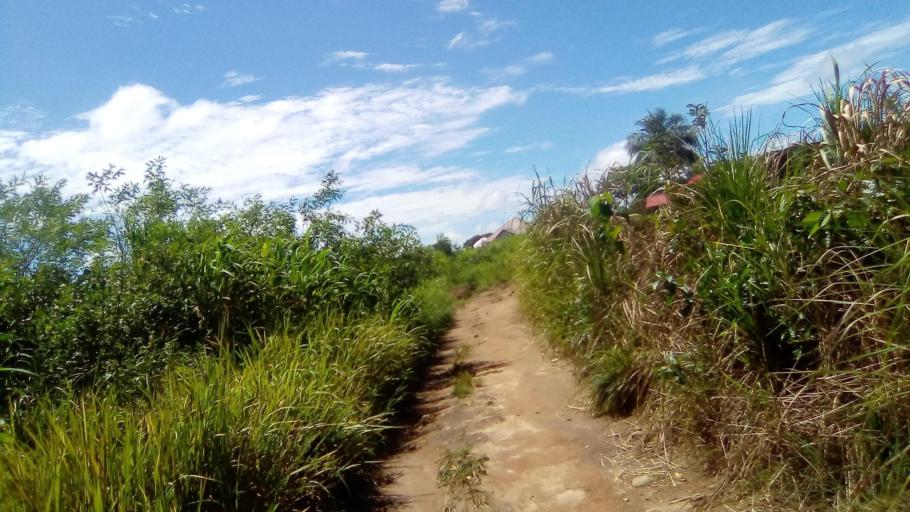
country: SL
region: Eastern Province
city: Simbakoro
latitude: 8.6326
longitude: -10.9990
